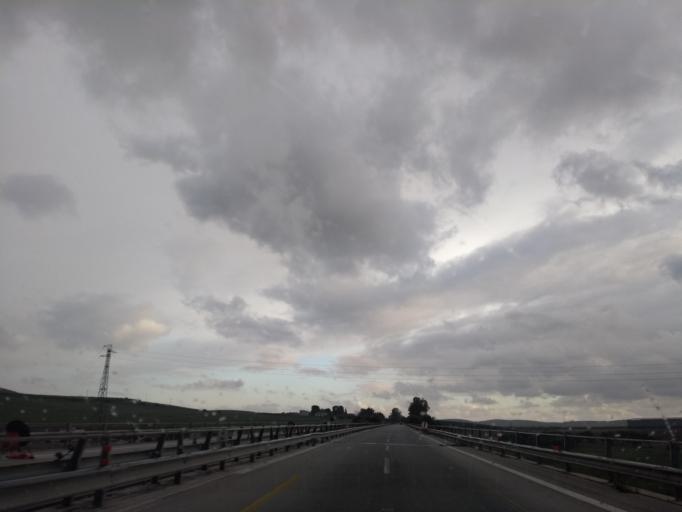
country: IT
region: Sicily
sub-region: Trapani
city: Paceco
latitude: 37.9933
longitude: 12.5965
